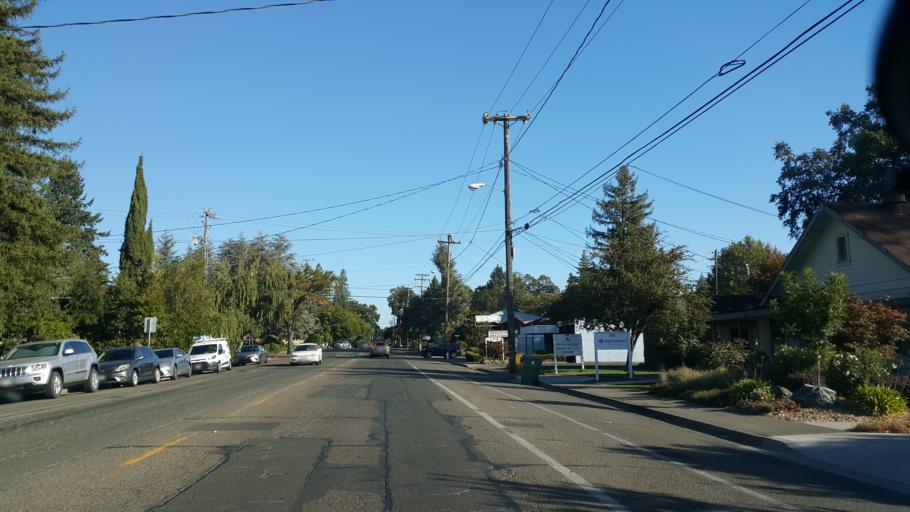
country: US
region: California
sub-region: Mendocino County
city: Ukiah
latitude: 39.1440
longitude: -123.2111
